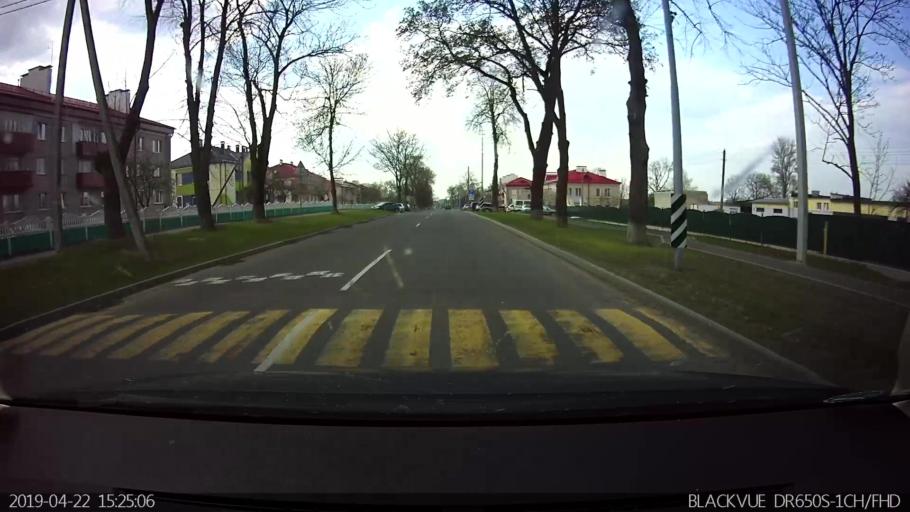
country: BY
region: Brest
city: Vysokaye
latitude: 52.3633
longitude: 23.3998
